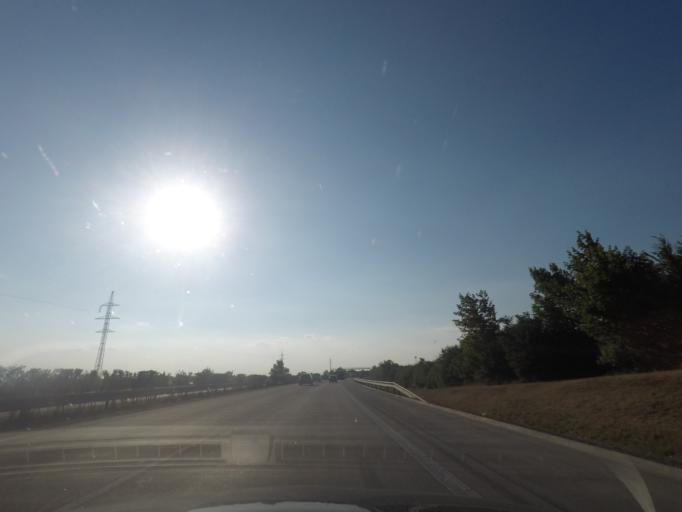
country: CZ
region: Olomoucky
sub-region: Okres Olomouc
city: Olomouc
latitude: 49.5496
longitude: 17.2364
